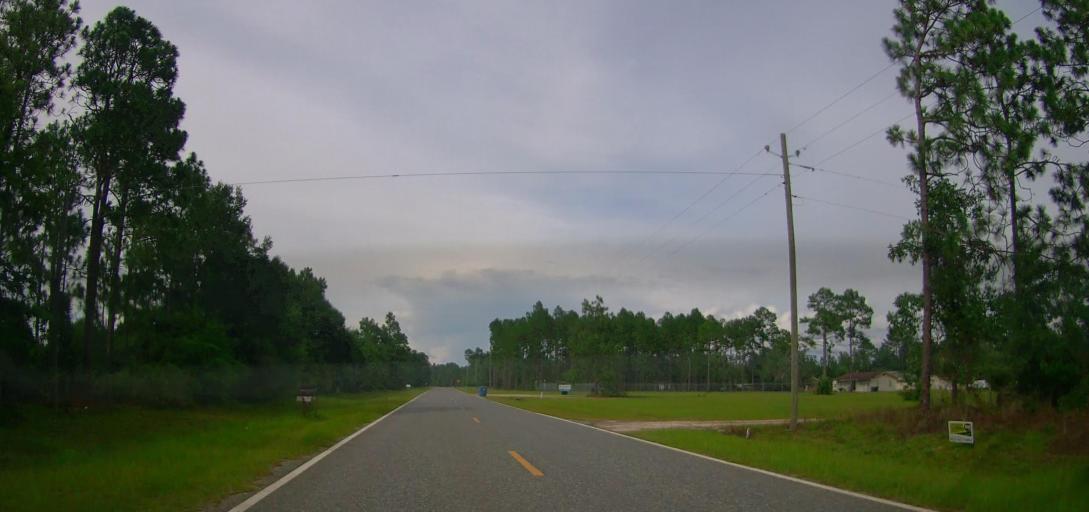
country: US
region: Georgia
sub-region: Wayne County
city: Jesup
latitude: 31.6679
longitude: -81.9109
